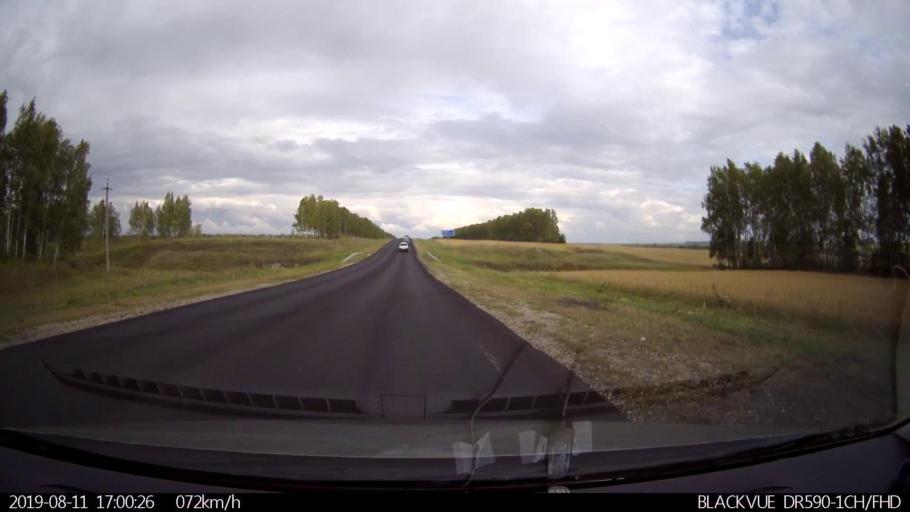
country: RU
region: Ulyanovsk
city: Mayna
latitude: 54.3104
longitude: 47.6794
